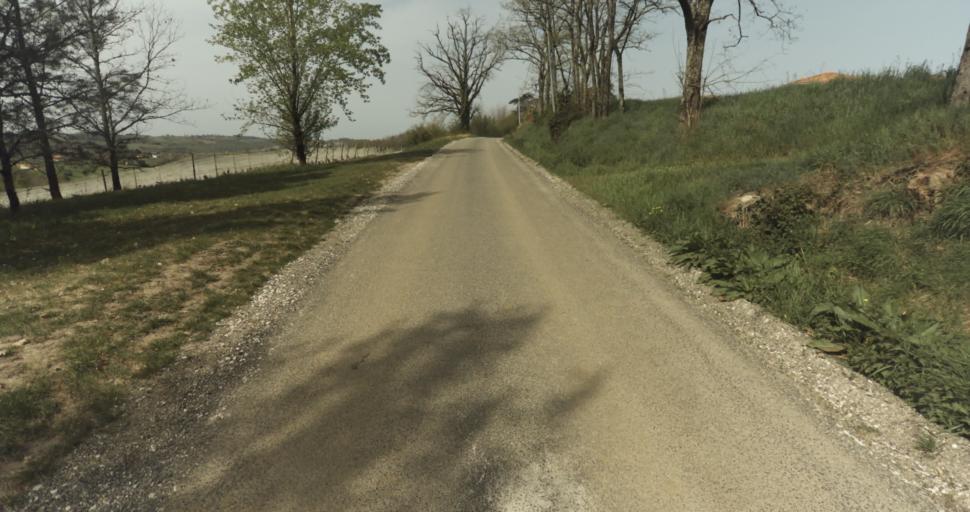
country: FR
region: Midi-Pyrenees
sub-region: Departement du Tarn-et-Garonne
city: Moissac
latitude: 44.1174
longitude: 1.0707
